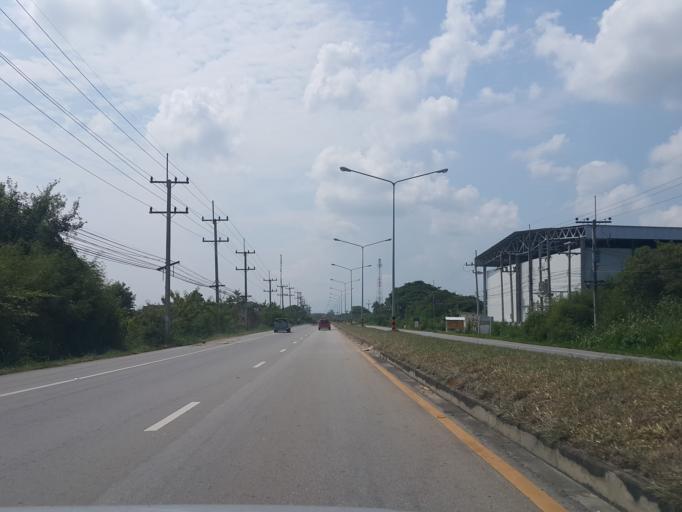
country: TH
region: Chiang Mai
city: Doi Lo
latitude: 18.5061
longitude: 98.8281
